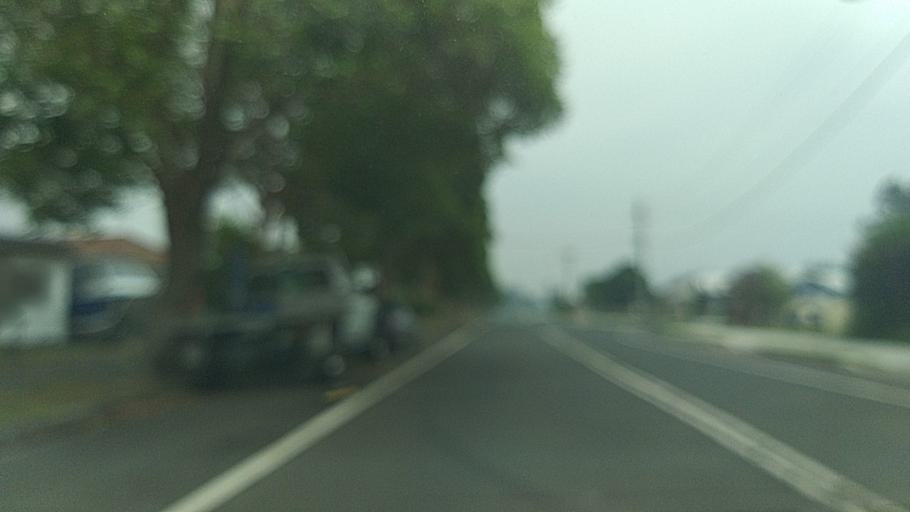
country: AU
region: New South Wales
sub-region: Shellharbour
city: Albion Park Rail
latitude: -34.5668
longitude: 150.7955
